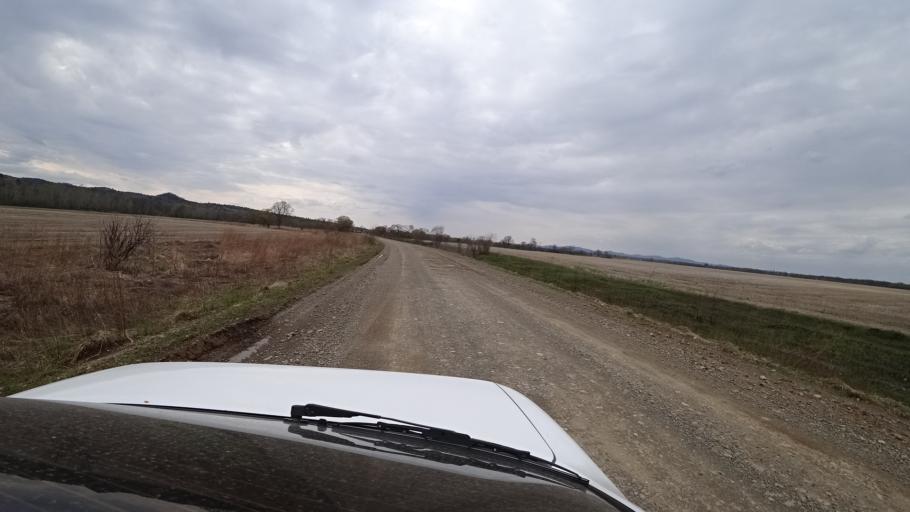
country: RU
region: Primorskiy
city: Novopokrovka
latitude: 45.4891
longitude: 134.4623
